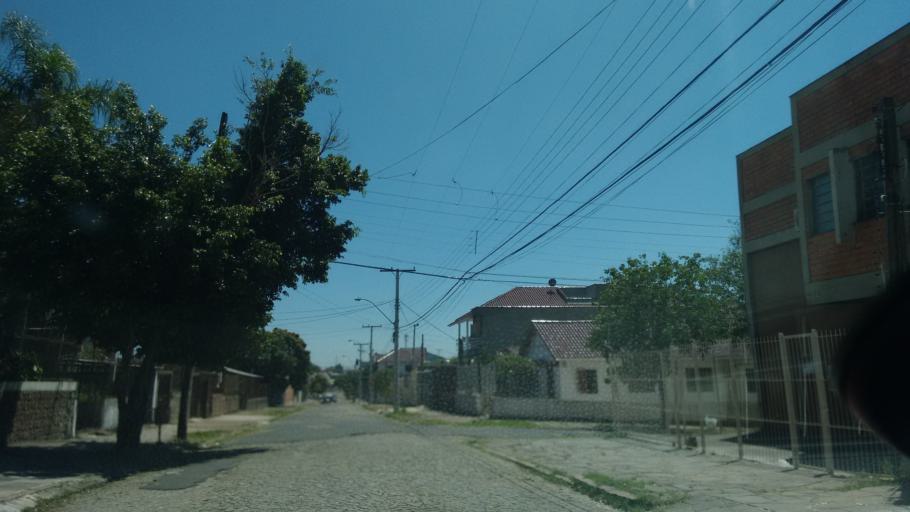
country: BR
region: Rio Grande do Sul
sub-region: Cachoeirinha
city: Cachoeirinha
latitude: -29.9999
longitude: -51.1288
